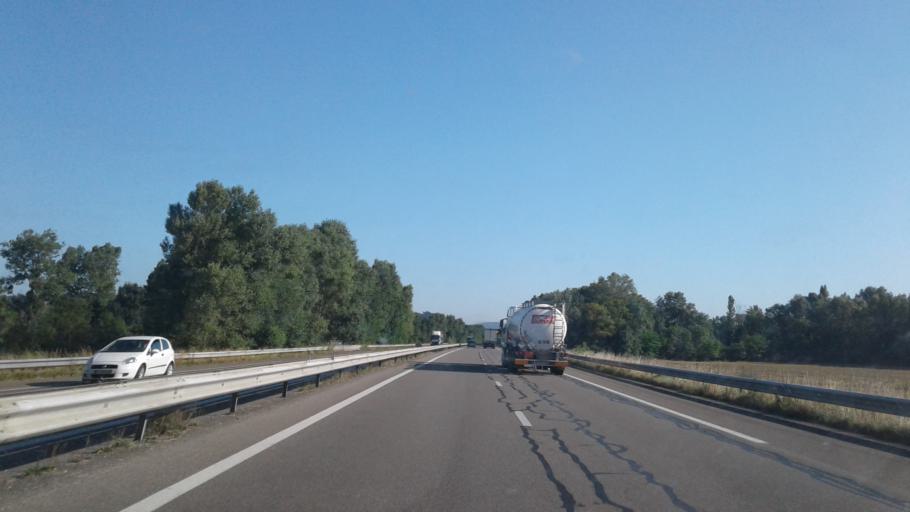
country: FR
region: Rhone-Alpes
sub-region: Departement de l'Ain
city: Priay
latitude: 46.0154
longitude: 5.3128
